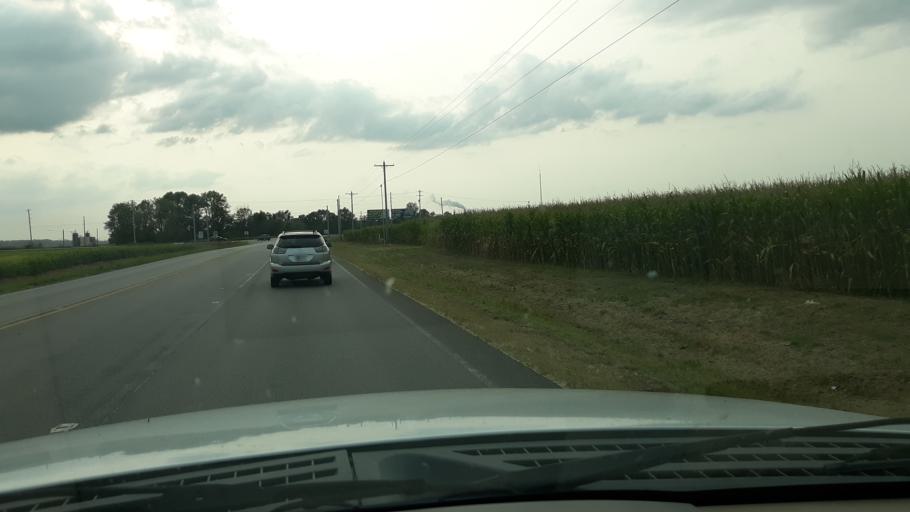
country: US
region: Indiana
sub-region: Gibson County
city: Owensville
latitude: 38.3559
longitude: -87.6843
